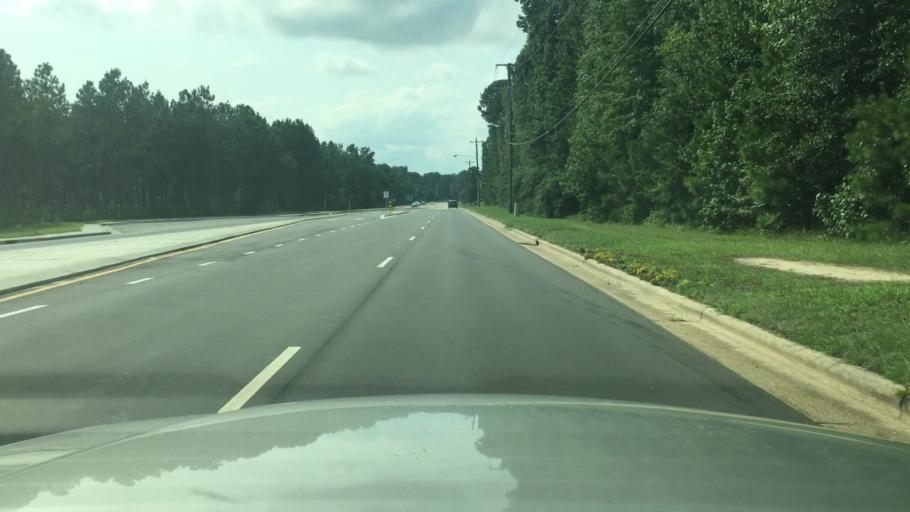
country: US
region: North Carolina
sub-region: Cumberland County
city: Vander
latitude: 35.0100
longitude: -78.8294
